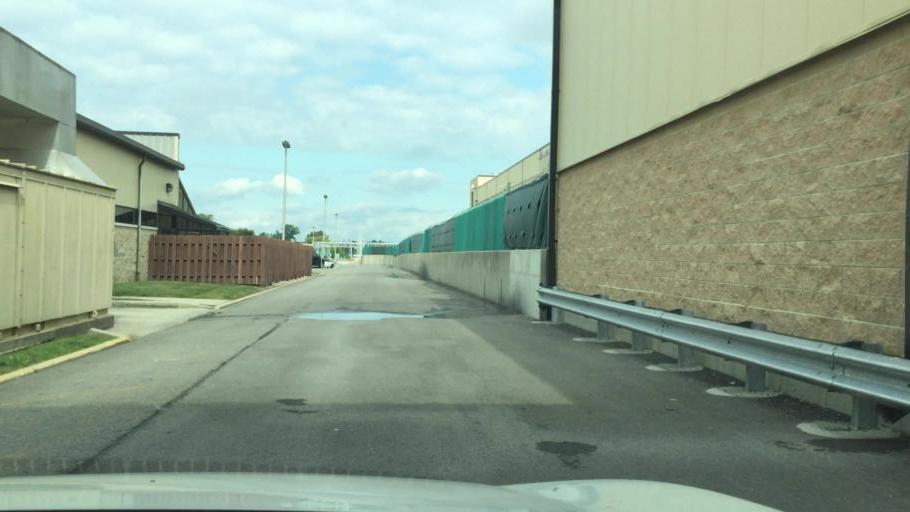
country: US
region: Ohio
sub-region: Champaign County
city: North Lewisburg
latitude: 40.2774
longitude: -83.5103
